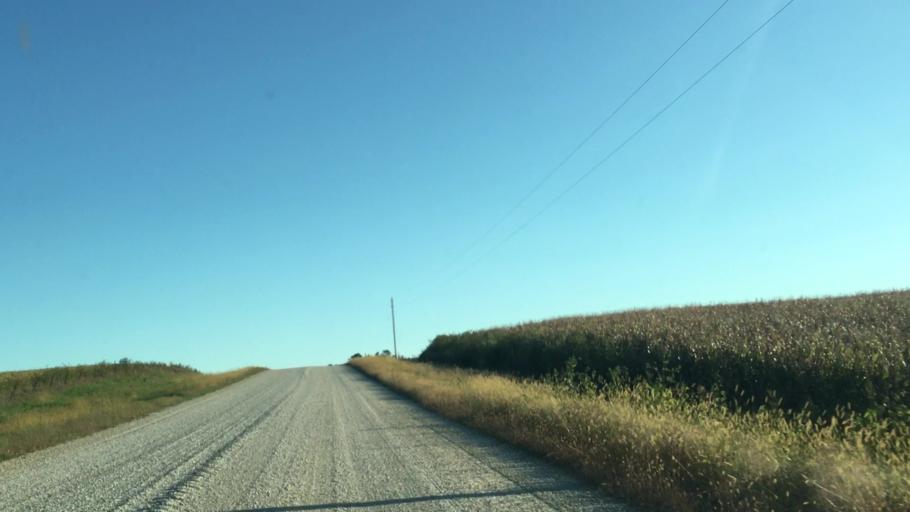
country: US
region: Minnesota
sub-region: Fillmore County
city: Preston
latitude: 43.8130
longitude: -92.0396
